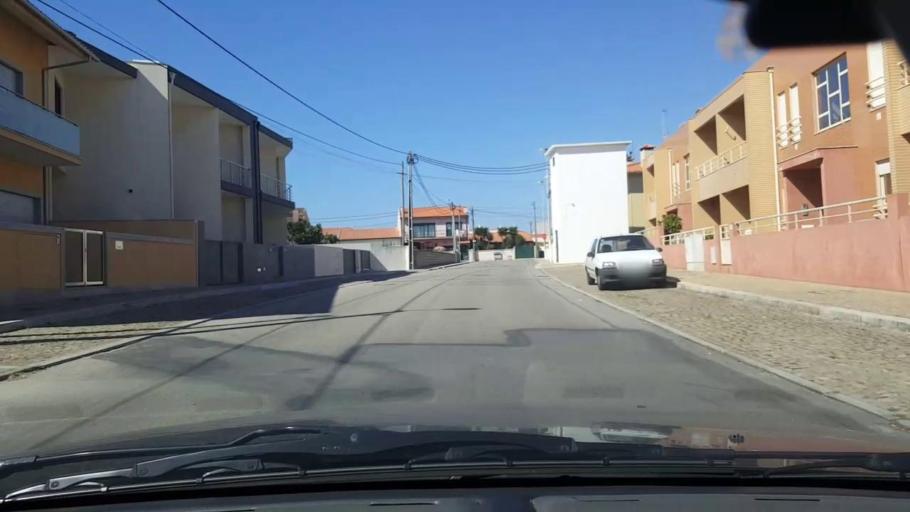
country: PT
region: Porto
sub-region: Matosinhos
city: Lavra
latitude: 41.2957
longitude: -8.7324
